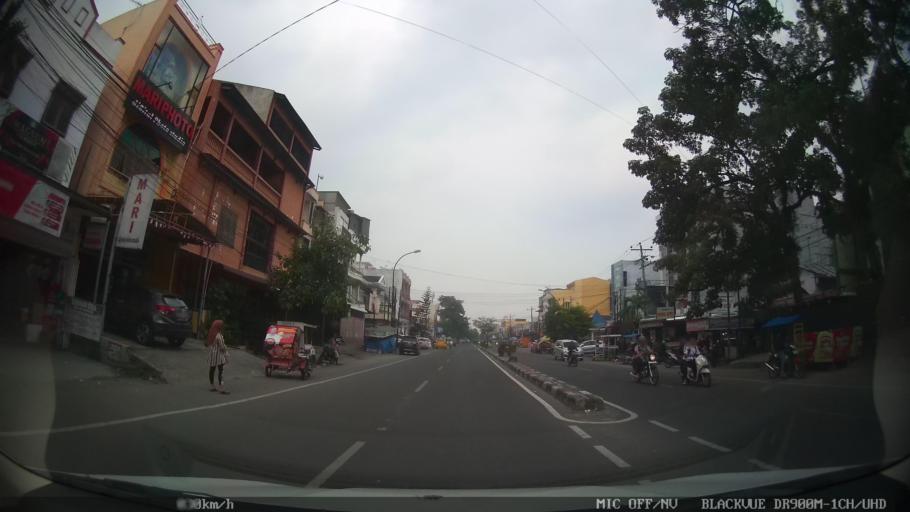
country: ID
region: North Sumatra
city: Medan
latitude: 3.5692
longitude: 98.7030
